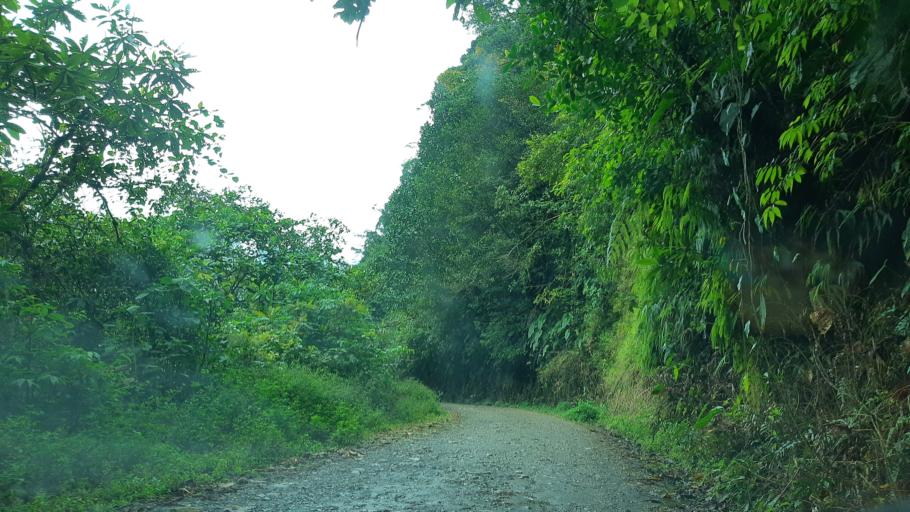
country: CO
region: Boyaca
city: Santa Maria
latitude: 4.8995
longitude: -73.3027
